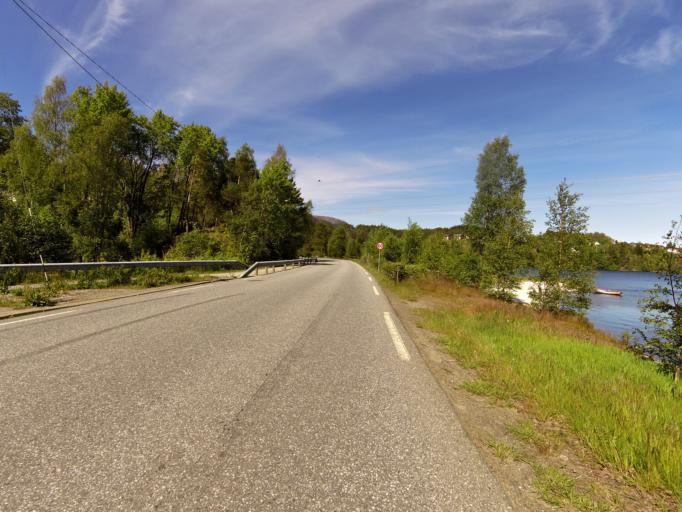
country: NO
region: Hordaland
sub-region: Stord
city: Sagvag
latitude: 59.7843
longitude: 5.4143
